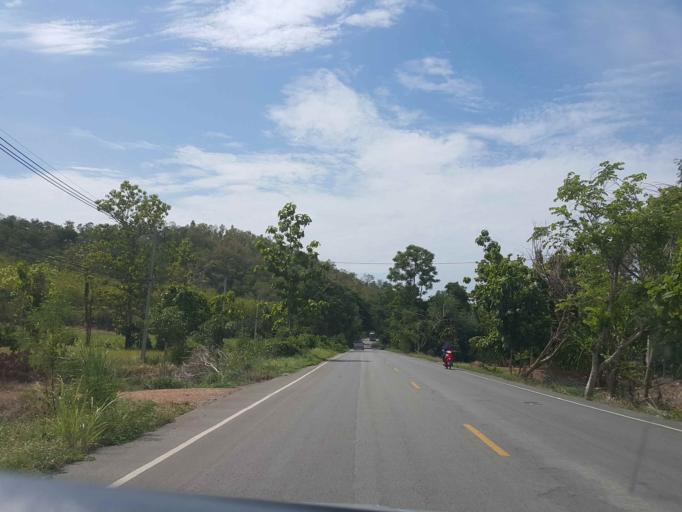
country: TH
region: Sukhothai
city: Thung Saliam
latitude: 17.3412
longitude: 99.4714
